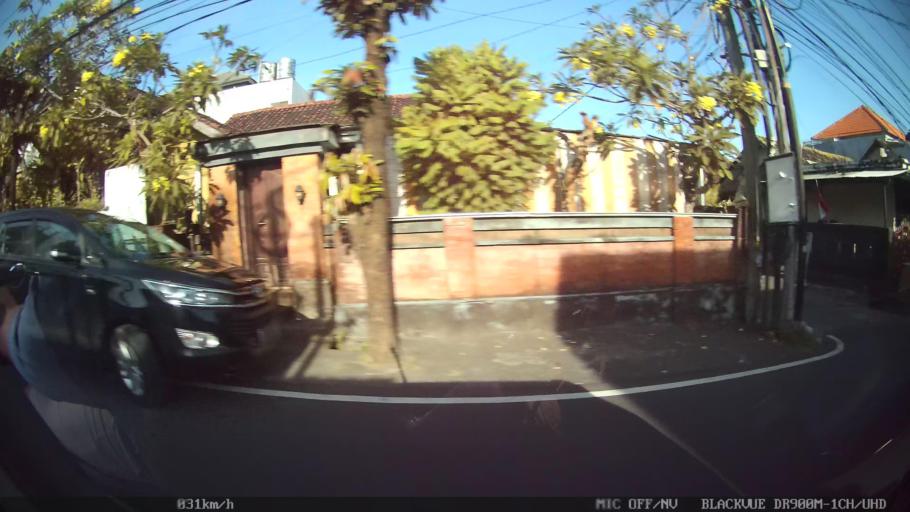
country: ID
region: Bali
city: Jimbaran
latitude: -8.8004
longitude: 115.1852
